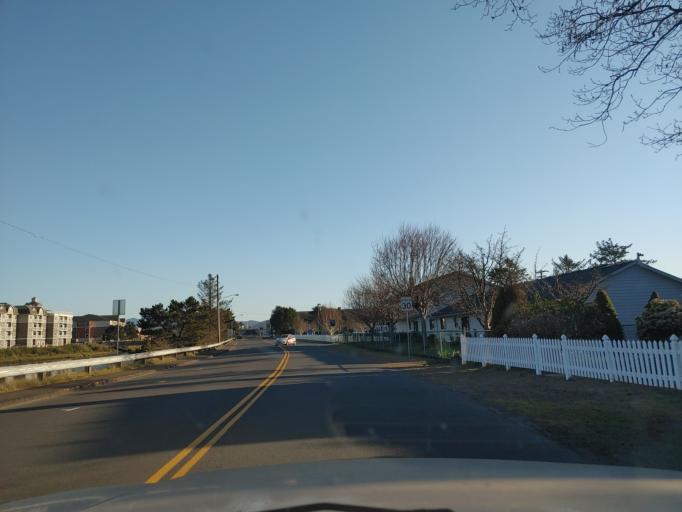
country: US
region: Oregon
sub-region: Clatsop County
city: Seaside
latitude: 45.9970
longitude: -123.9244
